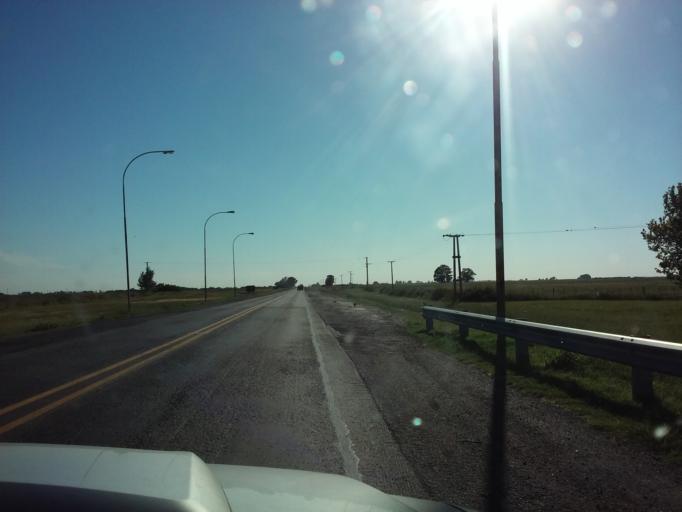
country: AR
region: Buenos Aires
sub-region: Partido de Trenque Lauquen
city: Trenque Lauquen
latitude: -35.9177
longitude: -62.5553
